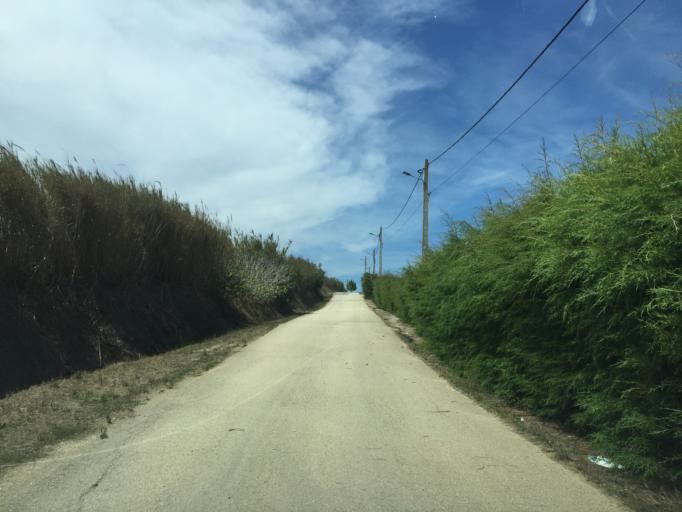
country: PT
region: Lisbon
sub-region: Lourinha
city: Lourinha
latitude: 39.2047
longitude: -9.3384
